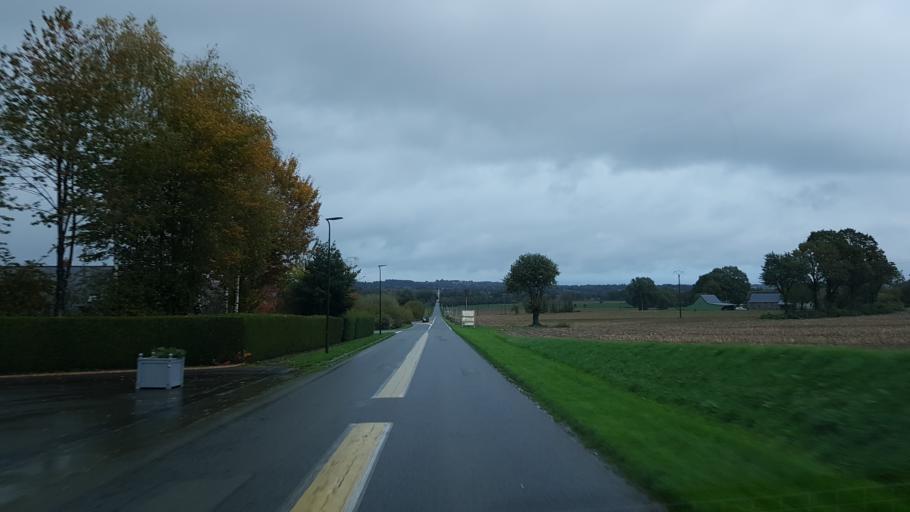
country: FR
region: Brittany
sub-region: Departement d'Ille-et-Vilaine
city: Chatillon-en-Vendelais
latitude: 48.1800
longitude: -1.1124
